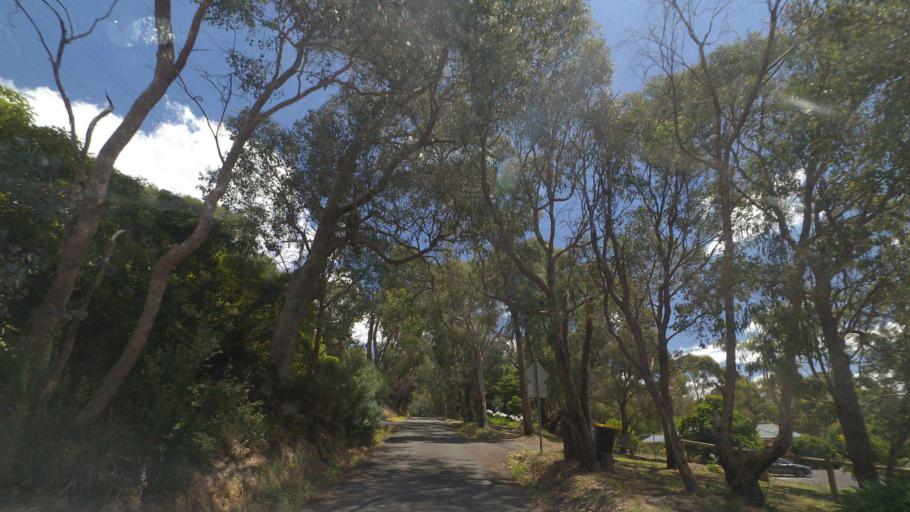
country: AU
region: Victoria
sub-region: Yarra Ranges
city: Chirnside Park
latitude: -37.7326
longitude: 145.2770
